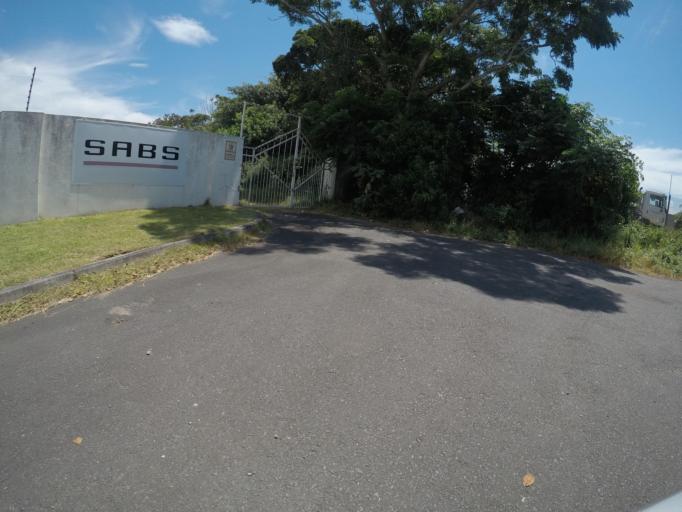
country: ZA
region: Eastern Cape
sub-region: Buffalo City Metropolitan Municipality
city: East London
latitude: -33.0365
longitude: 27.8433
